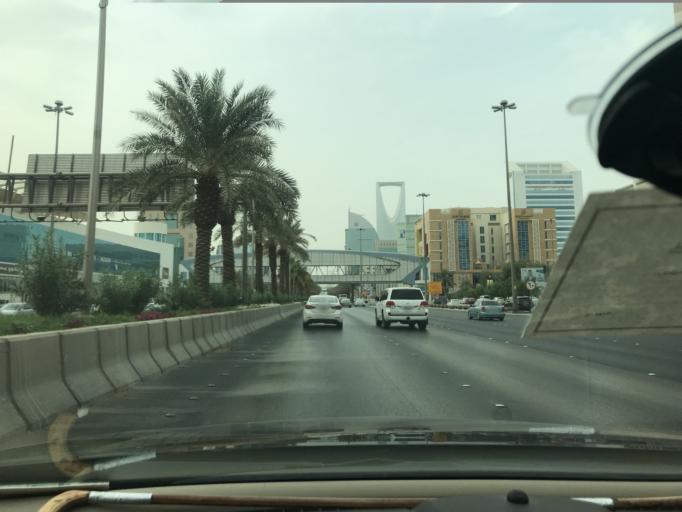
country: SA
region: Ar Riyad
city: Riyadh
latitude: 24.6985
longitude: 46.6789
